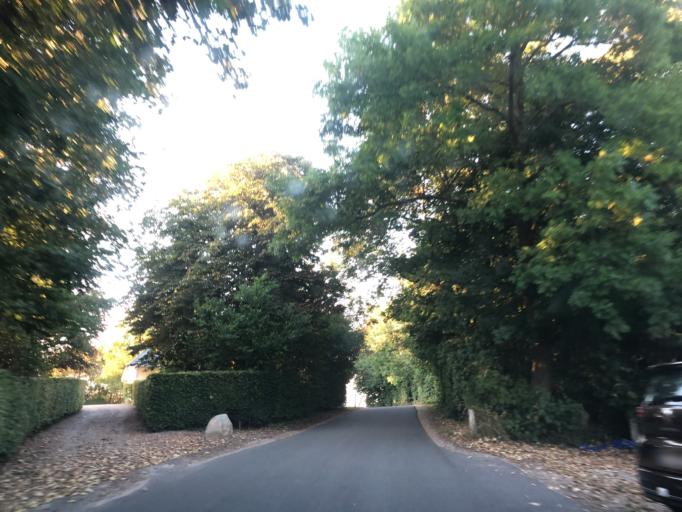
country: DK
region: Central Jutland
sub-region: Holstebro Kommune
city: Holstebro
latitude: 56.3894
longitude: 8.6837
